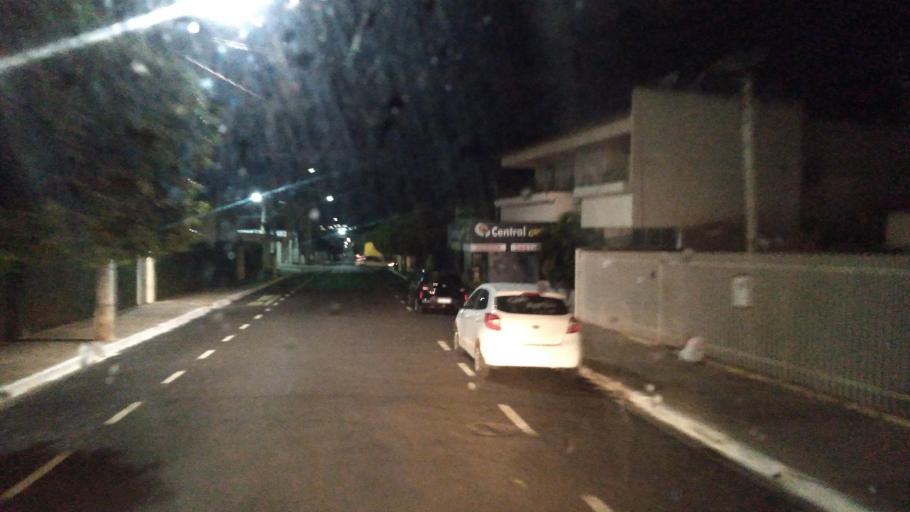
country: BR
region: Goias
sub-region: Mineiros
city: Mineiros
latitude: -17.5653
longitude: -52.5559
